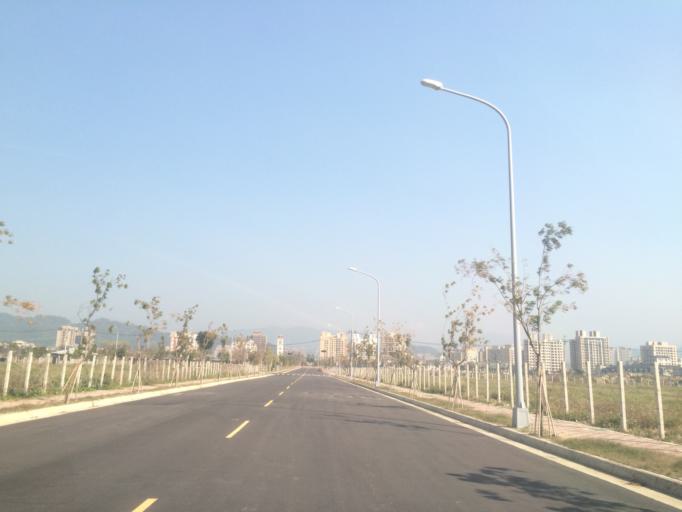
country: TW
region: Taiwan
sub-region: Taichung City
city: Taichung
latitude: 24.1782
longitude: 120.7042
